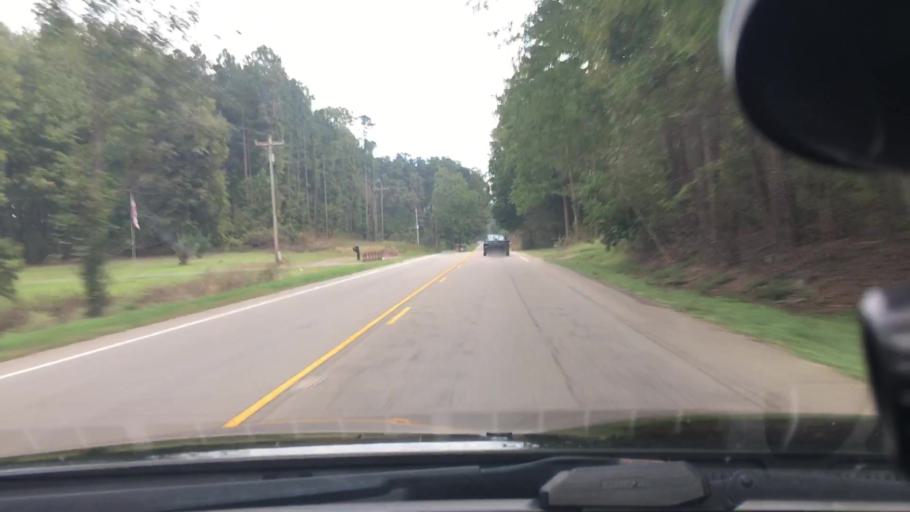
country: US
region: North Carolina
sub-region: Moore County
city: Robbins
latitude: 35.3944
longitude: -79.5268
